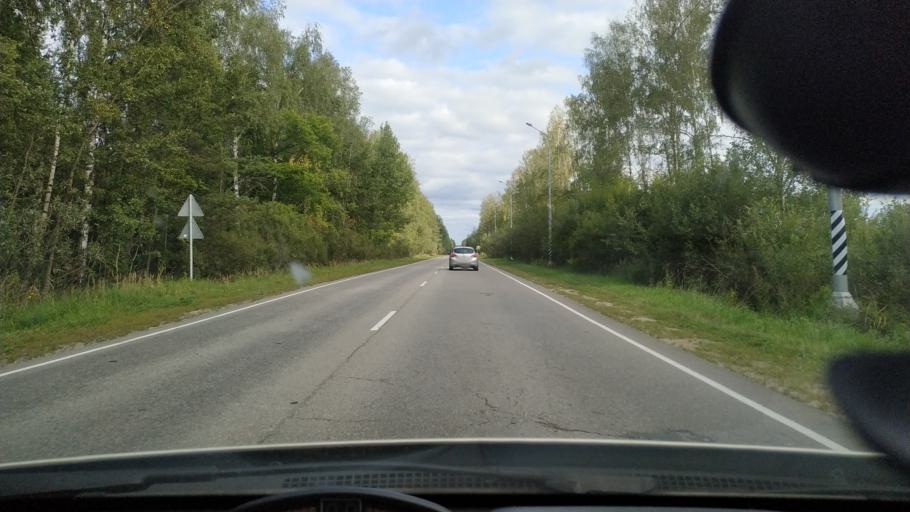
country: RU
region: Moskovskaya
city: Likino-Dulevo
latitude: 55.7290
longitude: 39.0177
